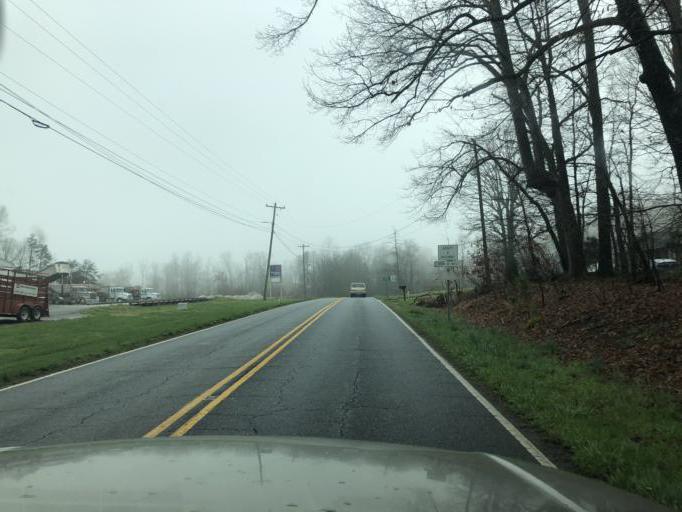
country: US
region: North Carolina
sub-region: Gaston County
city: Cherryville
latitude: 35.3651
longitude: -81.4204
